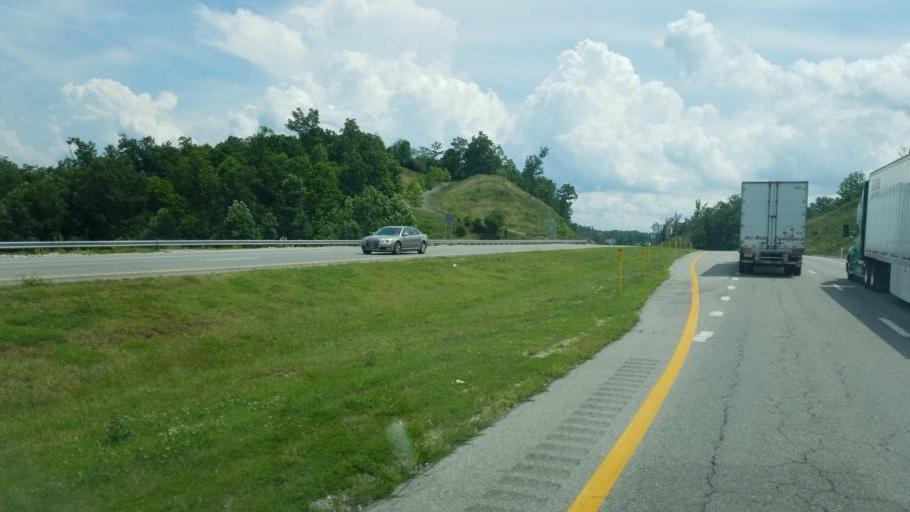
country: US
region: West Virginia
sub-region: Putnam County
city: Buffalo
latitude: 38.5621
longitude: -82.0114
